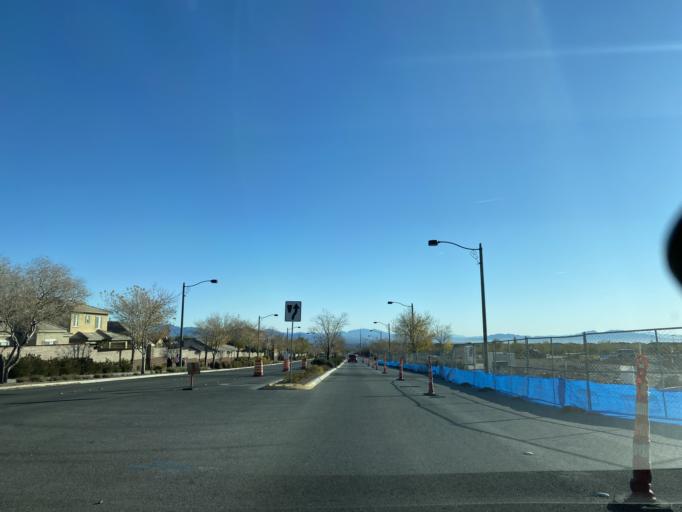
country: US
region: Nevada
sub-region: Clark County
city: Summerlin South
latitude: 36.2992
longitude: -115.3230
